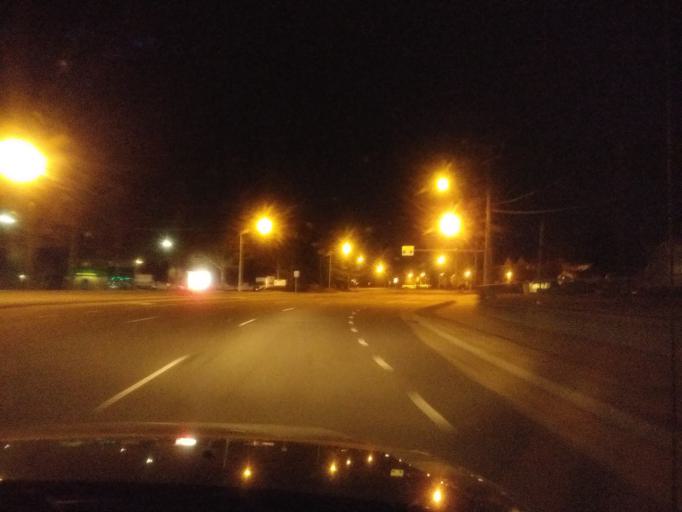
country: US
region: Virginia
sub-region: City of Chesapeake
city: Chesapeake
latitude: 36.7798
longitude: -76.1932
